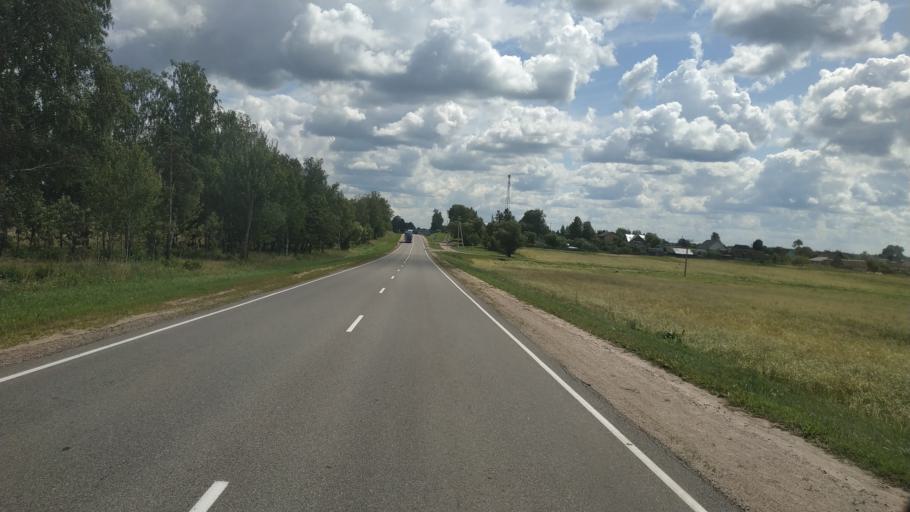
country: BY
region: Mogilev
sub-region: Mahilyowski Rayon
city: Veyno
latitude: 53.8171
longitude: 30.4446
